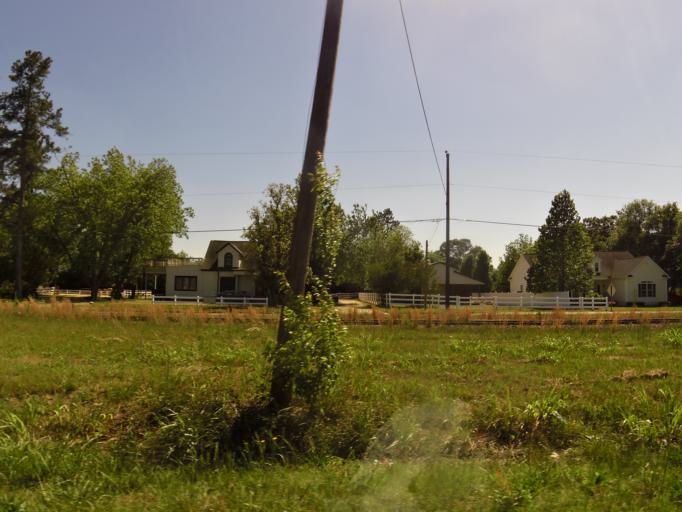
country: US
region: South Carolina
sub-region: Aiken County
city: Aiken
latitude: 33.5302
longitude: -81.6397
